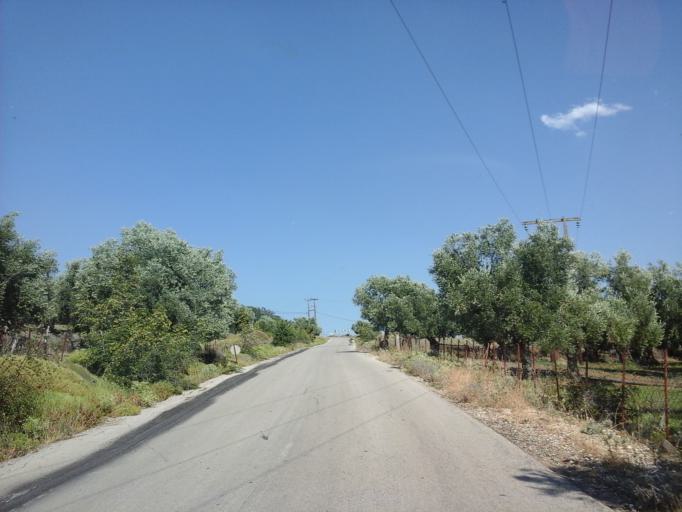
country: GR
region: East Macedonia and Thrace
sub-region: Nomos Evrou
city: Samothraki
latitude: 40.4273
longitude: 25.5177
